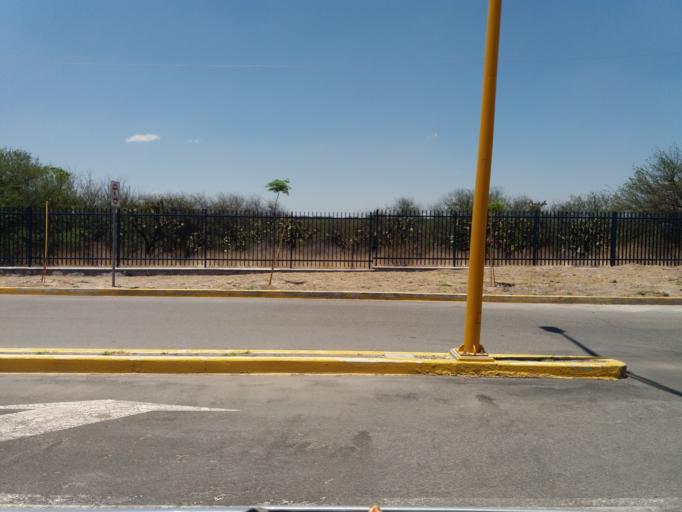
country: MX
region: Aguascalientes
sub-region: Aguascalientes
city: San Sebastian [Fraccionamiento]
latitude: 21.7924
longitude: -102.2900
